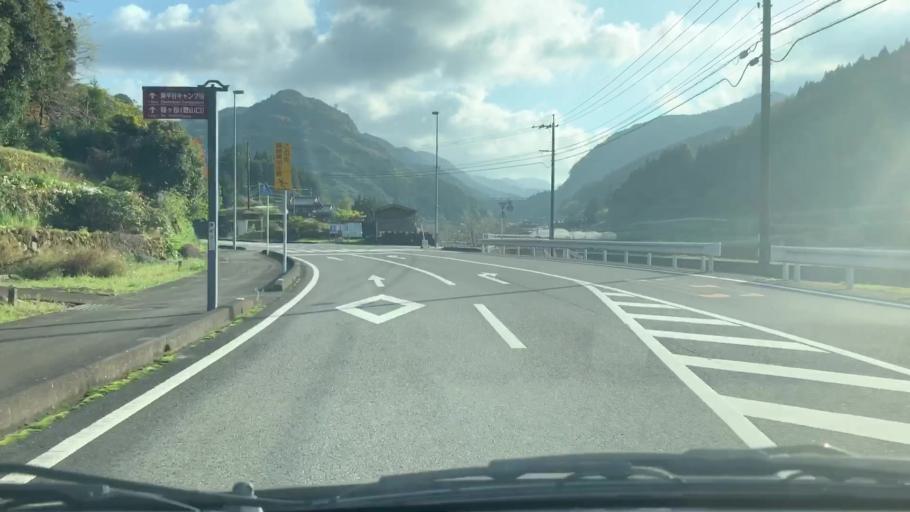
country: JP
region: Saga Prefecture
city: Kashima
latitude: 33.0575
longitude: 130.0705
